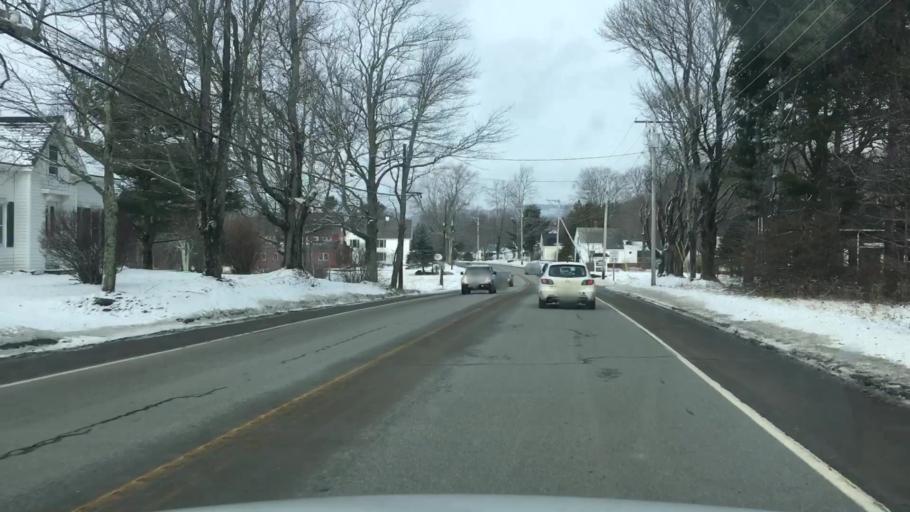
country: US
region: Maine
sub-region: Knox County
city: Rockport
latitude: 44.1728
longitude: -69.0797
